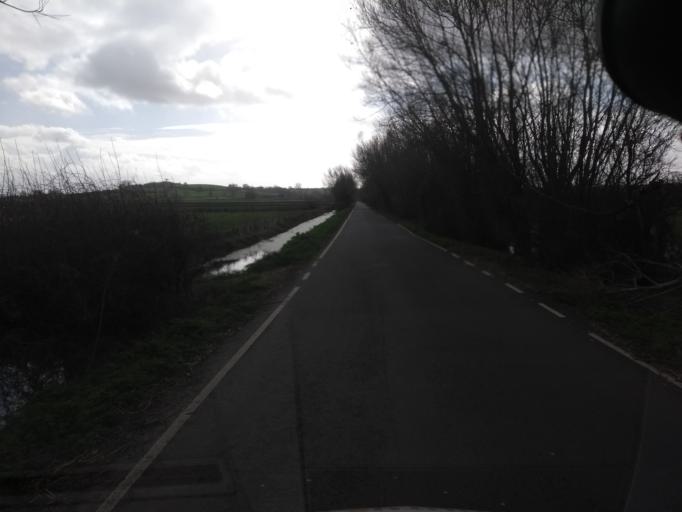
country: GB
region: England
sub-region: Somerset
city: Curry Rivel
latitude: 50.9893
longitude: -2.8526
